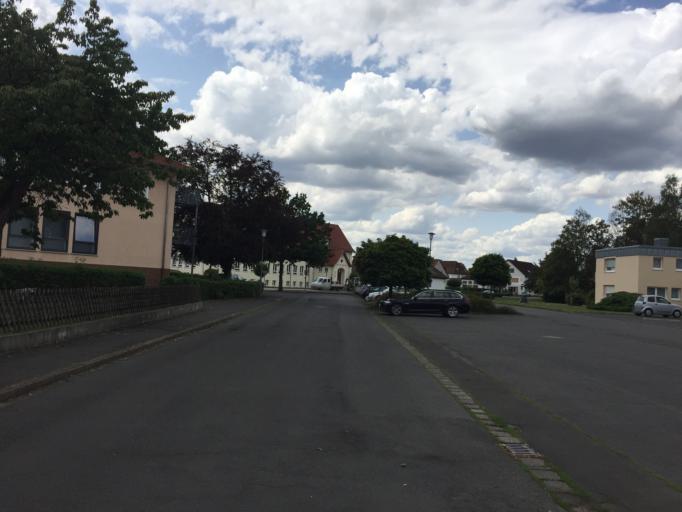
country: DE
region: Hesse
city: Schwalmstadt
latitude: 50.9138
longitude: 9.2407
